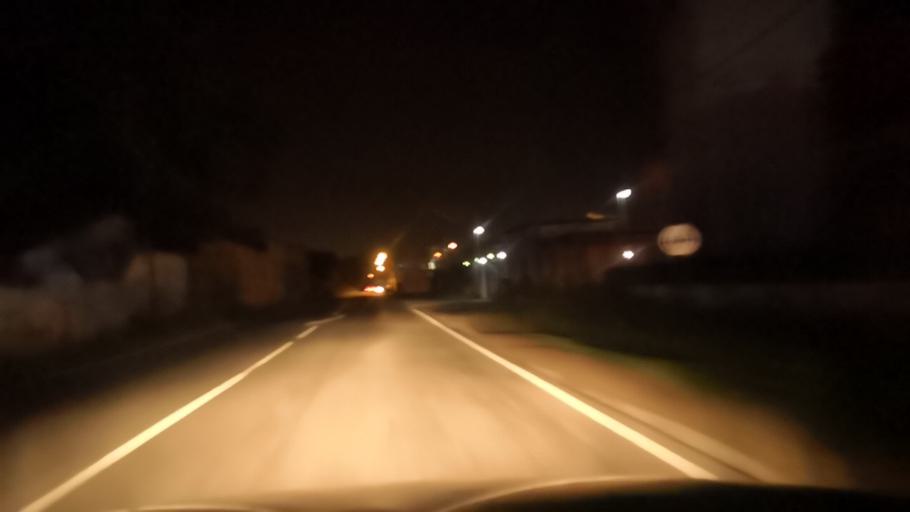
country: PT
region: Setubal
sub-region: Setubal
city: Setubal
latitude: 38.5118
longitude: -8.8564
